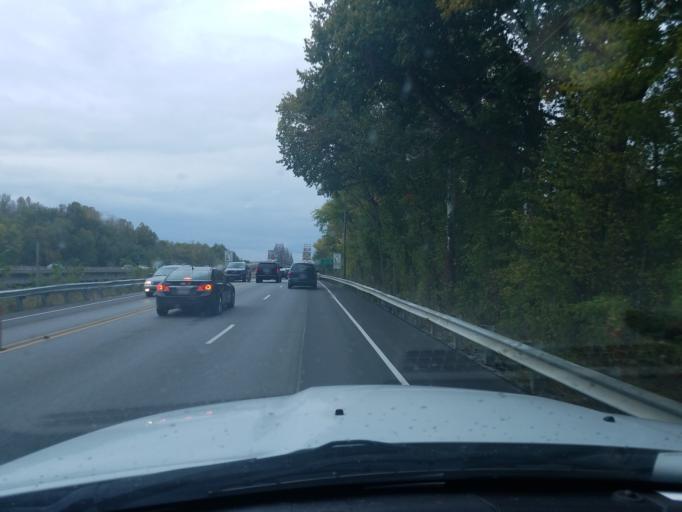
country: US
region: Kentucky
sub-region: Henderson County
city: Henderson
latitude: 37.8967
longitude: -87.5537
